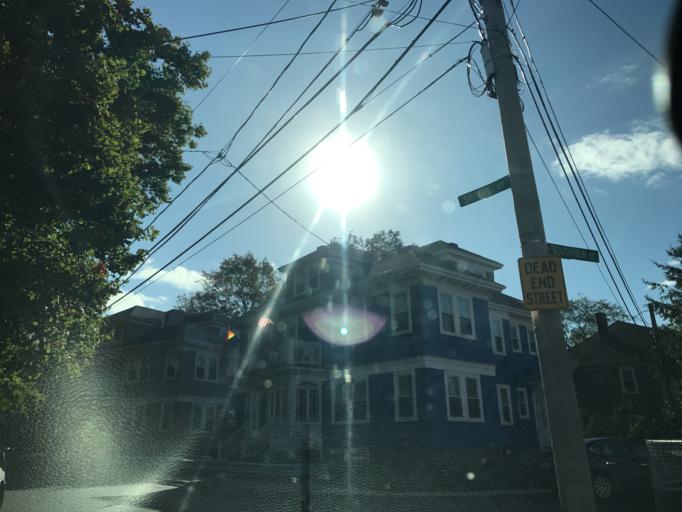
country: US
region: Massachusetts
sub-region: Suffolk County
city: South Boston
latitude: 42.3087
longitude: -71.0501
